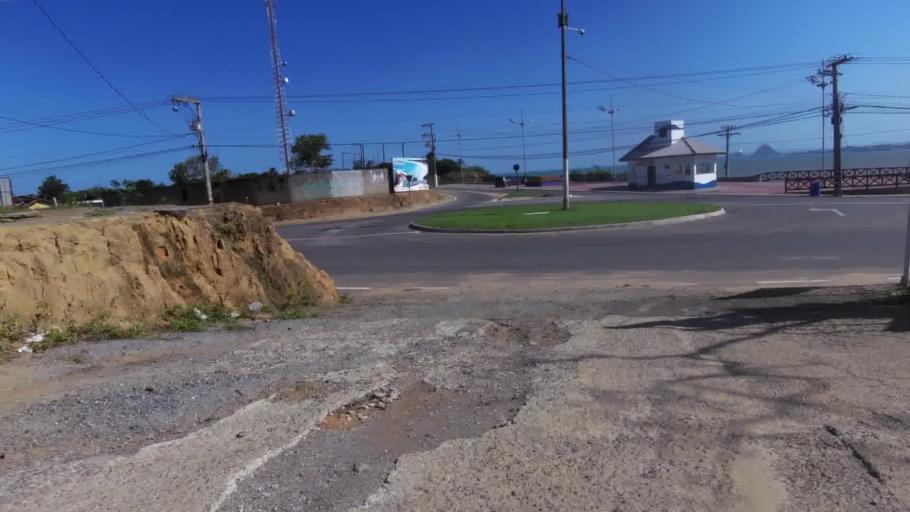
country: BR
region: Espirito Santo
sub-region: Piuma
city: Piuma
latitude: -20.8198
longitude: -40.6270
